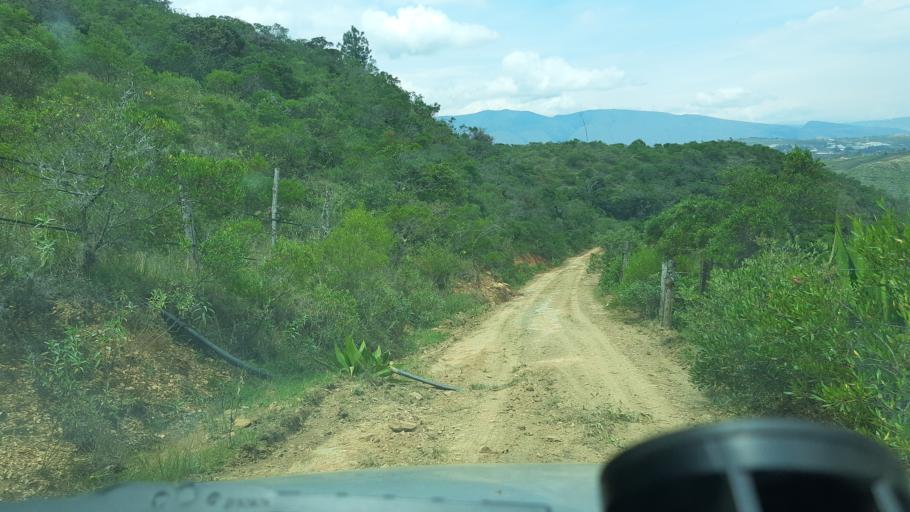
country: CO
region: Boyaca
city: Santa Sofia
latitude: 5.6962
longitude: -73.5804
